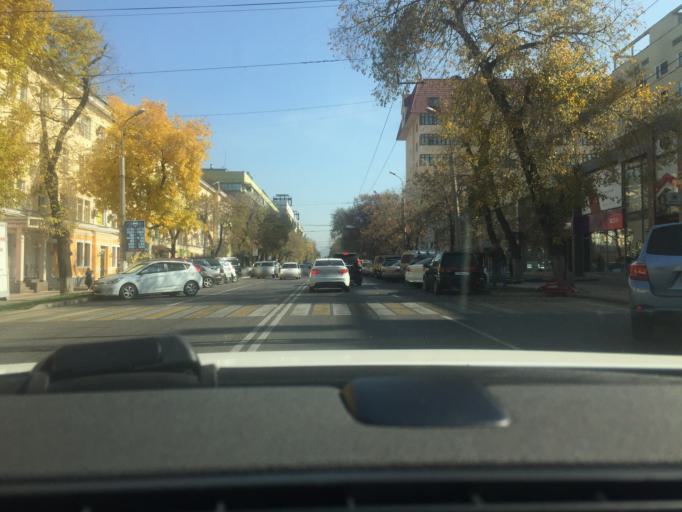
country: KZ
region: Almaty Qalasy
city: Almaty
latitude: 43.2598
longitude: 76.9427
